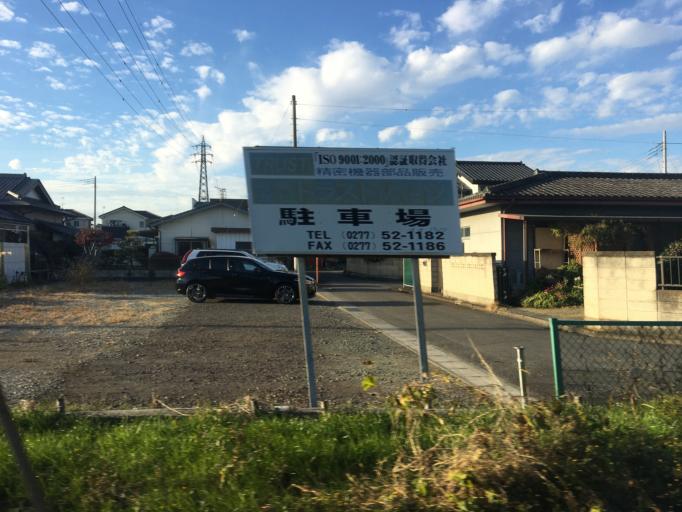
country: JP
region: Gunma
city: Kiryu
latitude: 36.4019
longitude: 139.3062
